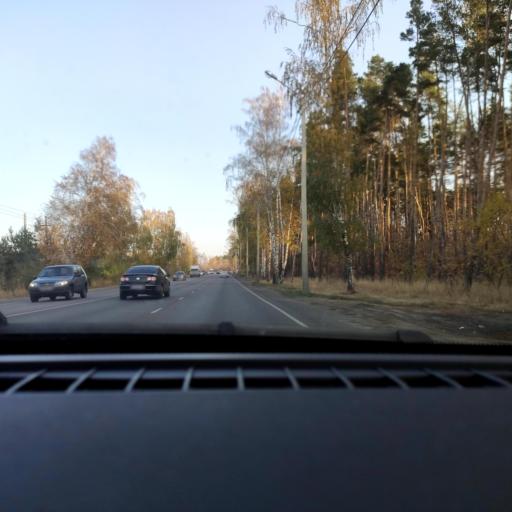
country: RU
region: Voronezj
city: Voronezh
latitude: 51.6765
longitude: 39.2733
